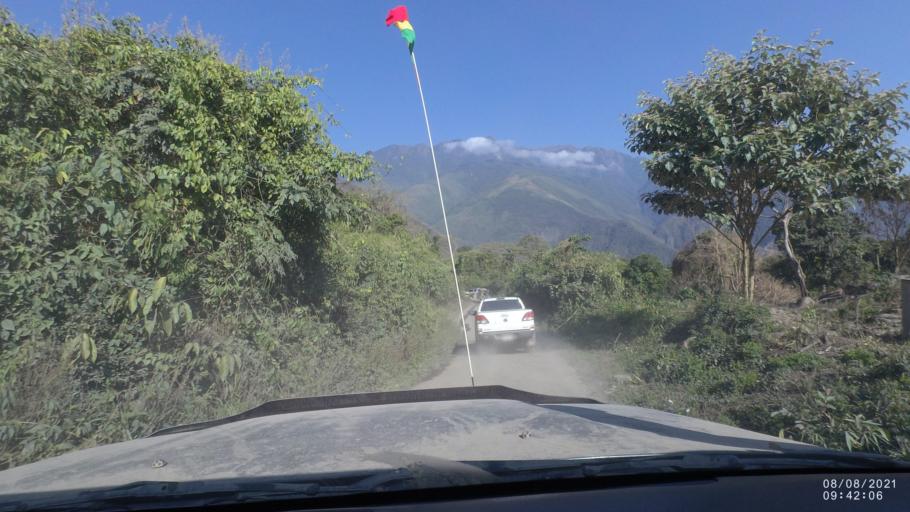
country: BO
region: La Paz
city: Quime
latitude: -16.6009
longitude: -66.7154
